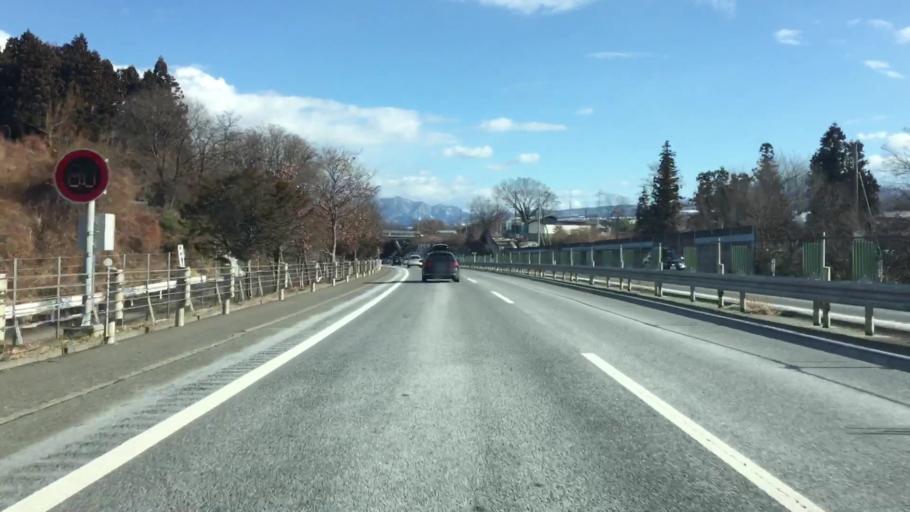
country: JP
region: Gunma
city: Numata
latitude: 36.6737
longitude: 139.0315
